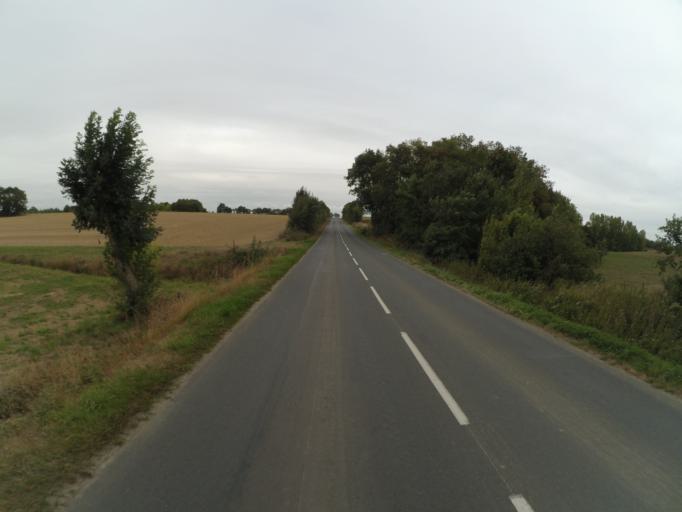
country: FR
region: Pays de la Loire
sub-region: Departement de la Vendee
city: Saint-Andre-Treize-Voies
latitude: 46.9227
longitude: -1.3948
